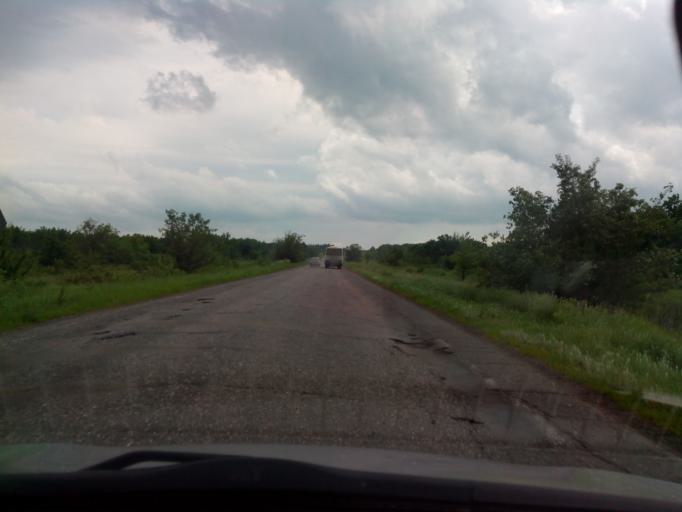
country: RU
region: Volgograd
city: Mikhaylovka
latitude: 49.9647
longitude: 43.0340
